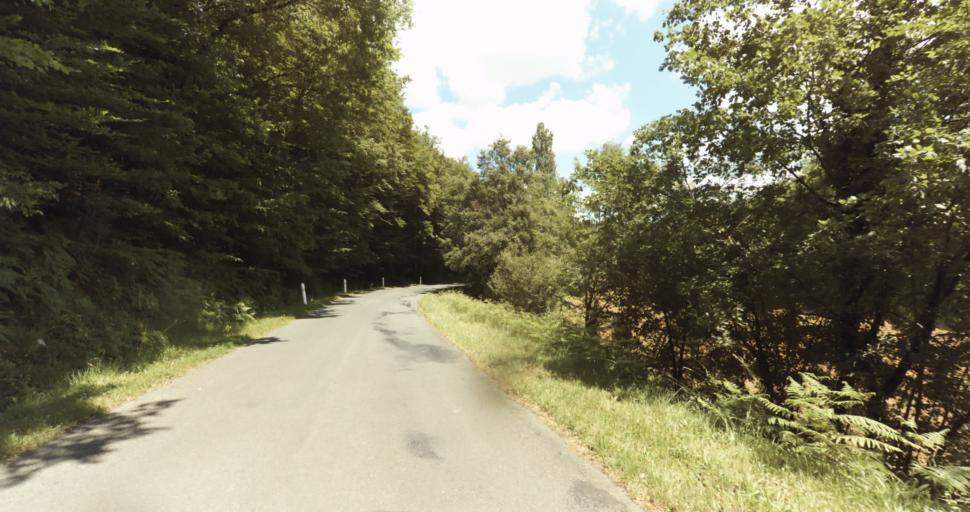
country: FR
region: Aquitaine
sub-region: Departement de la Dordogne
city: Beaumont-du-Perigord
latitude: 44.7693
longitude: 0.7538
